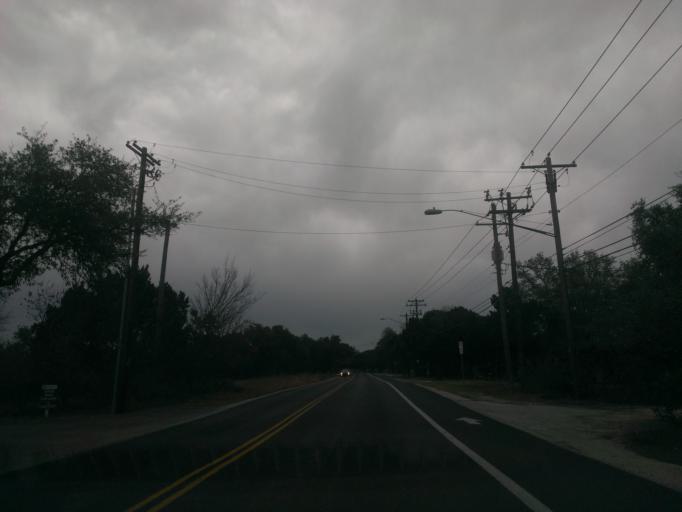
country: US
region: Texas
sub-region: Williamson County
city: Jollyville
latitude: 30.3799
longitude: -97.7653
